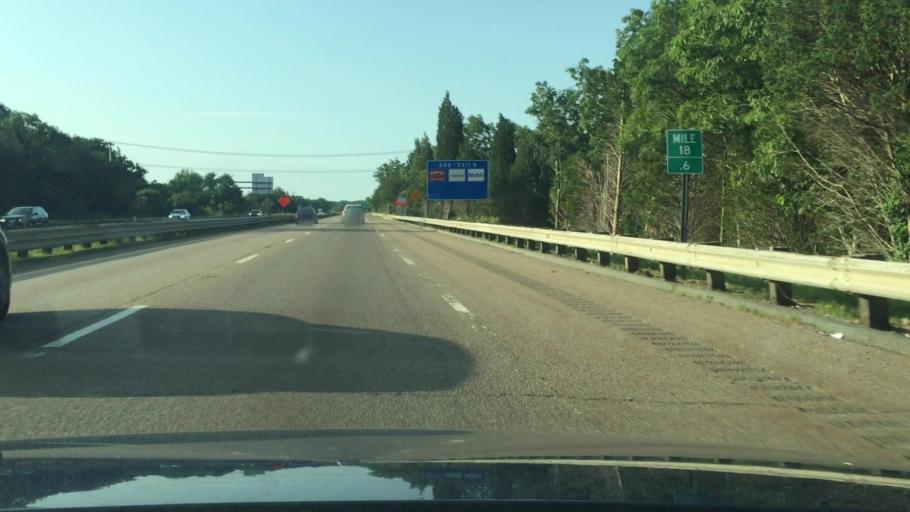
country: US
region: Massachusetts
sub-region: Plymouth County
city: Kingston
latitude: 41.9993
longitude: -70.7223
